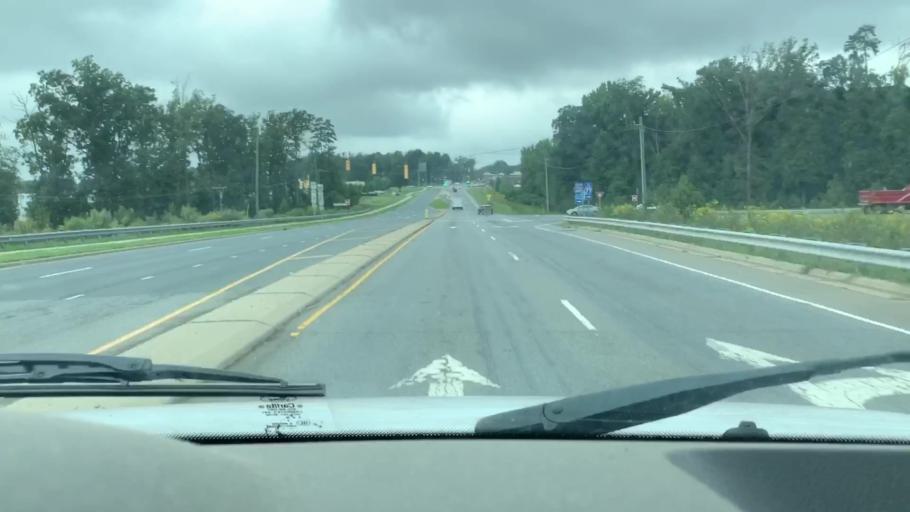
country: US
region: North Carolina
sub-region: Mecklenburg County
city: Huntersville
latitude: 35.3663
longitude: -80.8279
